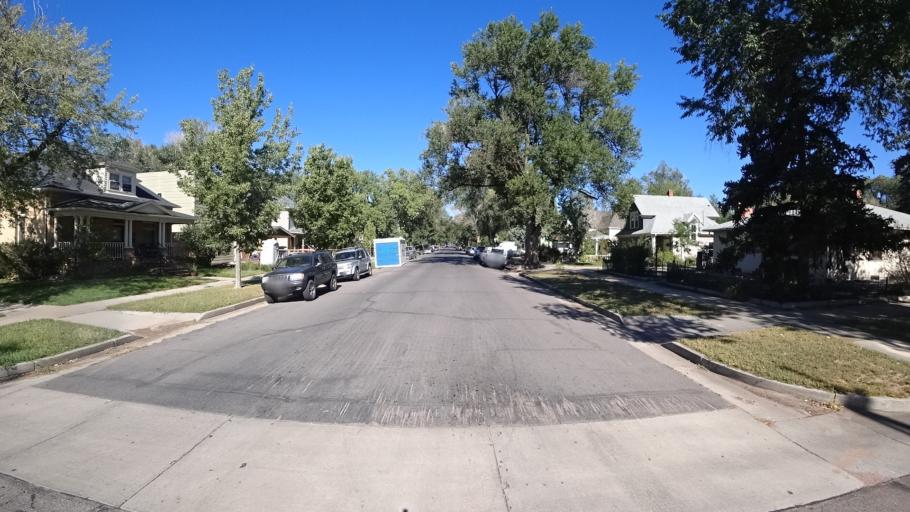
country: US
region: Colorado
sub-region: El Paso County
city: Colorado Springs
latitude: 38.8404
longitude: -104.8489
